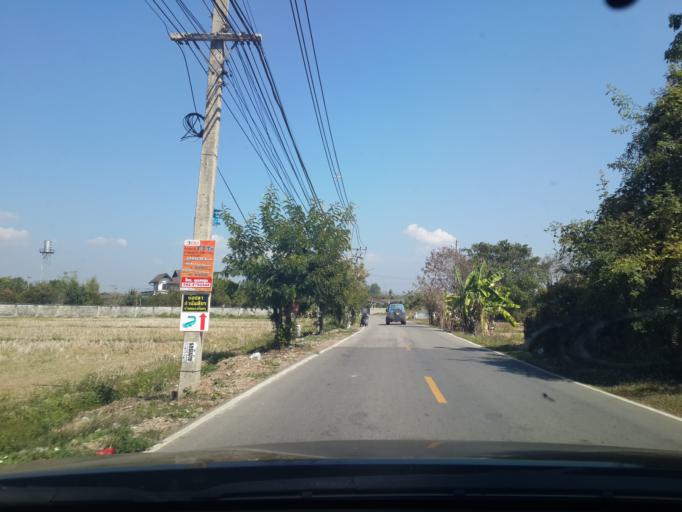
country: TH
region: Chiang Mai
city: San Sai
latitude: 18.8596
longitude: 99.0898
